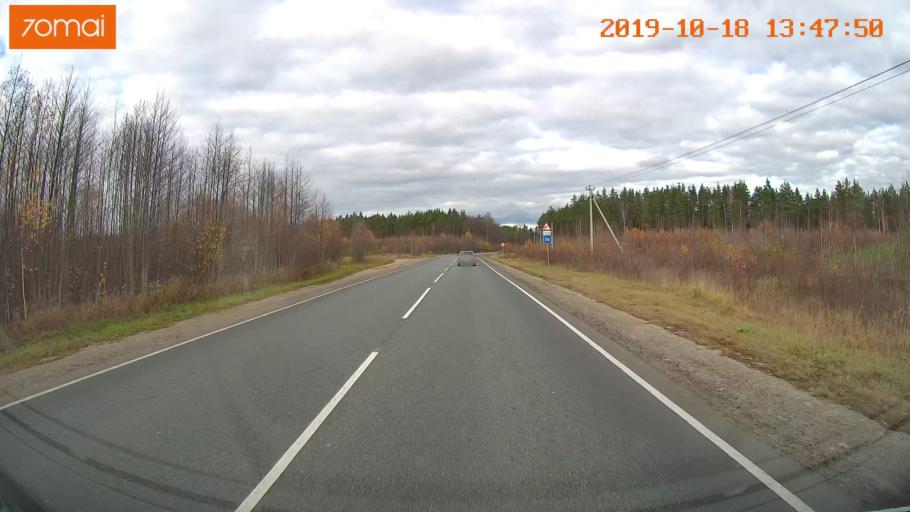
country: RU
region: Moskovskaya
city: Radovitskiy
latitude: 54.9809
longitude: 39.9515
